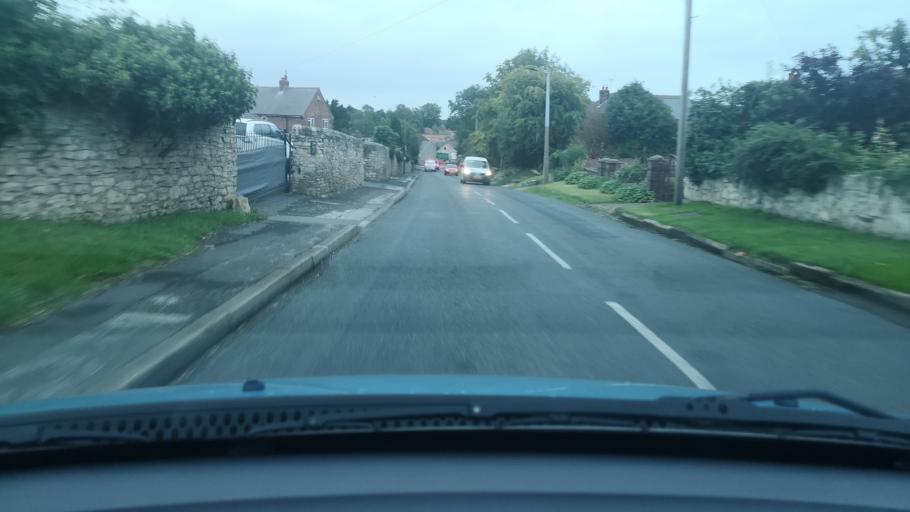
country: GB
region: England
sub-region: Doncaster
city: Campsall
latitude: 53.6166
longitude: -1.1846
